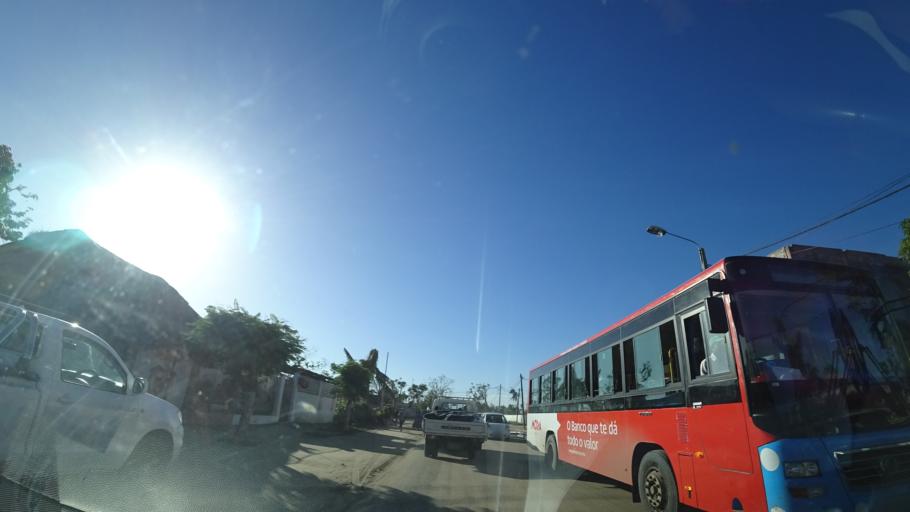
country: MZ
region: Sofala
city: Beira
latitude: -19.7789
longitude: 34.8721
